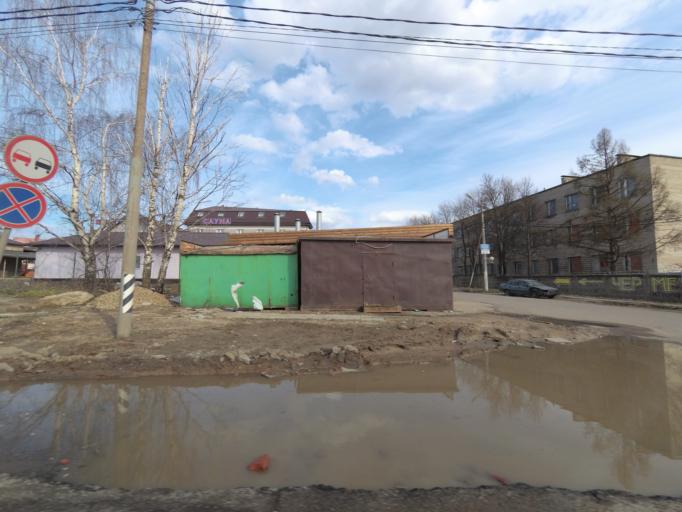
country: RU
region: Moskovskaya
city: Lobnya
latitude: 55.9907
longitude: 37.4163
